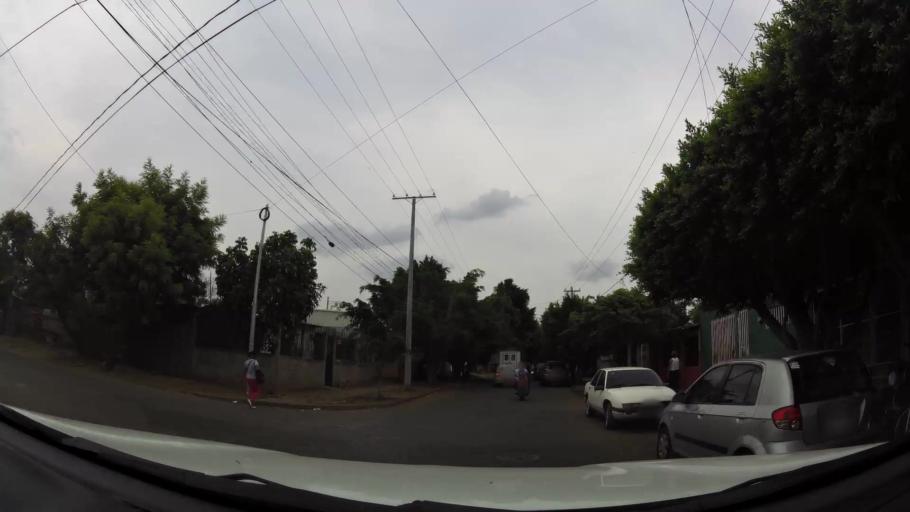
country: NI
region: Managua
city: Managua
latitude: 12.1240
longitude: -86.2386
